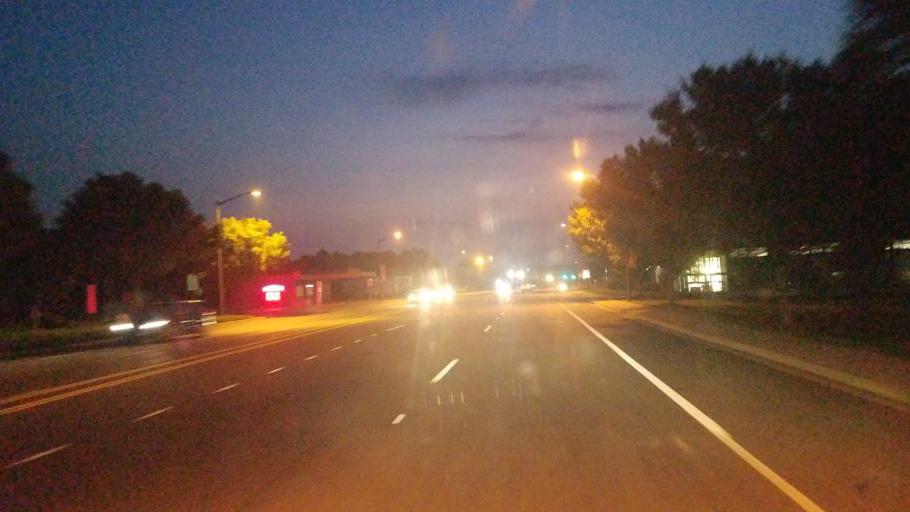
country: US
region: South Carolina
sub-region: York County
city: Fort Mill
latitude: 34.9773
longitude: -80.9822
